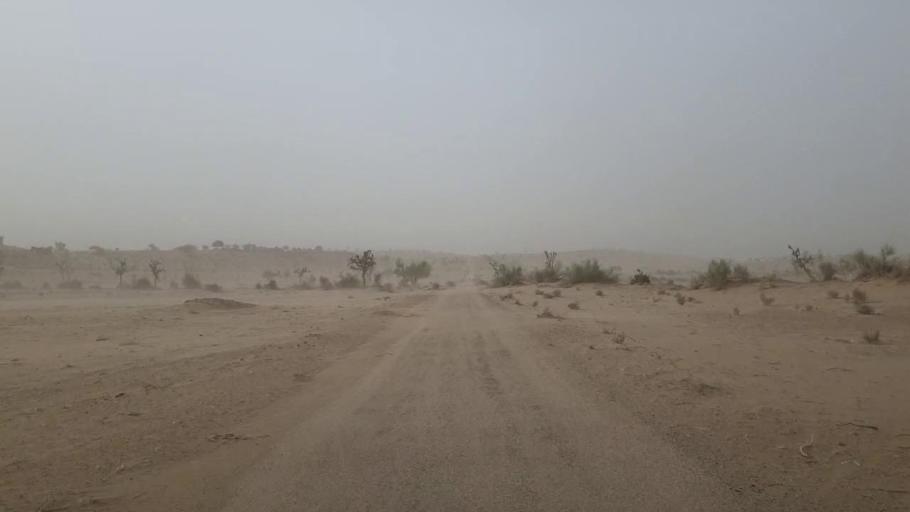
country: PK
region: Sindh
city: Islamkot
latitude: 24.5505
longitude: 70.3601
